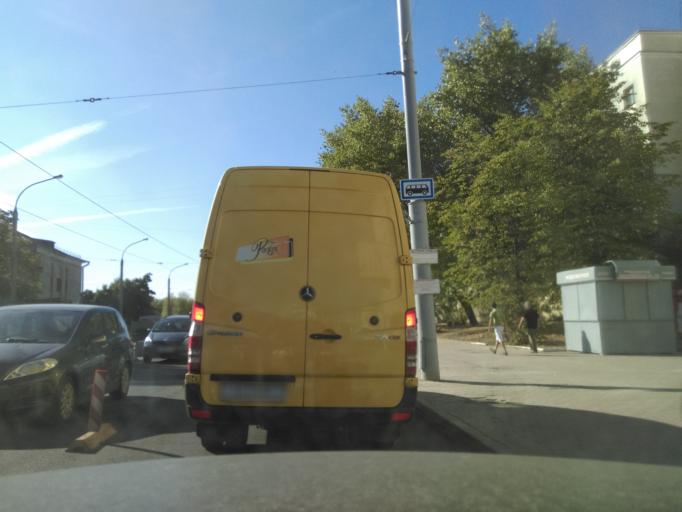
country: BY
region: Minsk
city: Minsk
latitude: 53.9037
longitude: 27.5989
